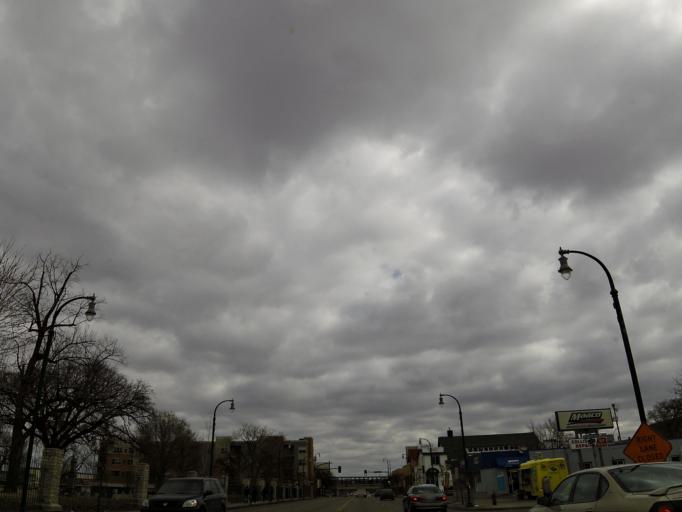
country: US
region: Minnesota
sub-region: Hennepin County
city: Minneapolis
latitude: 44.9484
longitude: -93.2440
